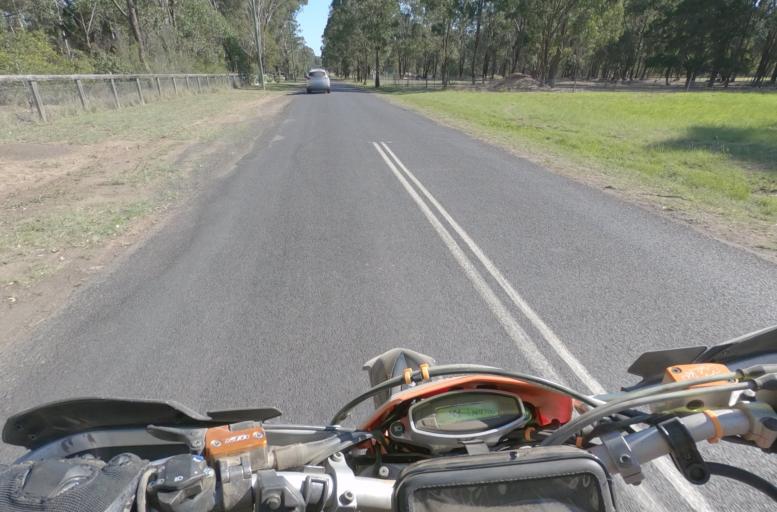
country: AU
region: New South Wales
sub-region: Hawkesbury
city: Pitt Town
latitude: -33.5814
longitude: 150.8773
